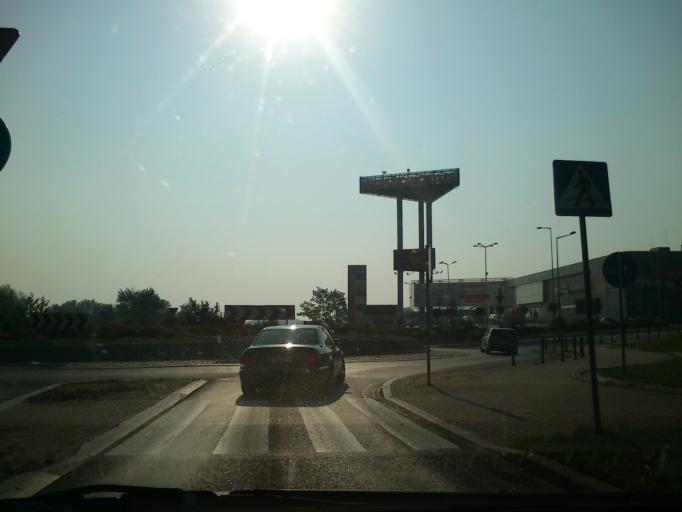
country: PL
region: Lower Silesian Voivodeship
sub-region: Powiat lubinski
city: Lubin
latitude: 51.3904
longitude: 16.2134
